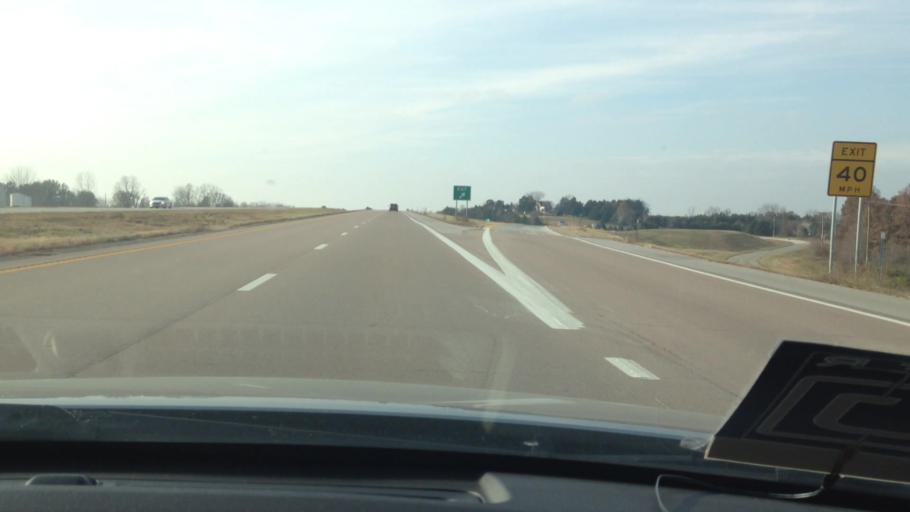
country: US
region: Missouri
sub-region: Cass County
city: Garden City
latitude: 38.4654
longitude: -93.9983
